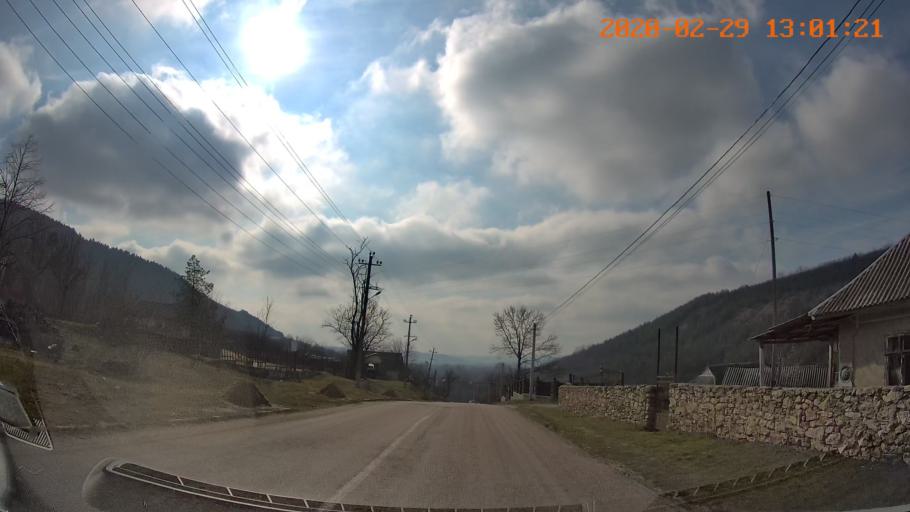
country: MD
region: Telenesti
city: Camenca
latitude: 48.0447
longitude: 28.7186
